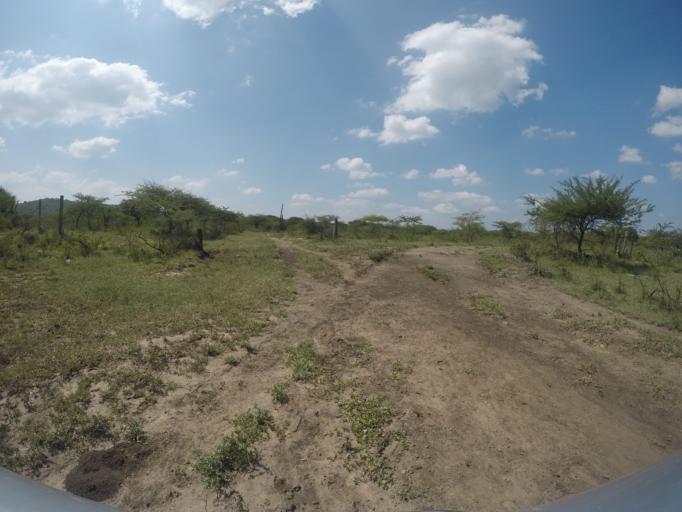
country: ZA
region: KwaZulu-Natal
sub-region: uThungulu District Municipality
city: Empangeni
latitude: -28.5858
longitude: 31.7421
